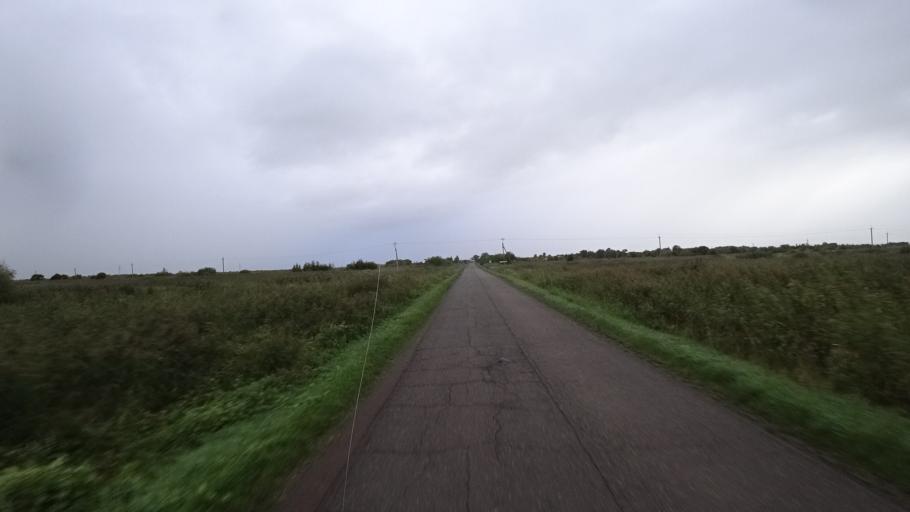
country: RU
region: Primorskiy
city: Chernigovka
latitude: 44.3933
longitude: 132.5286
